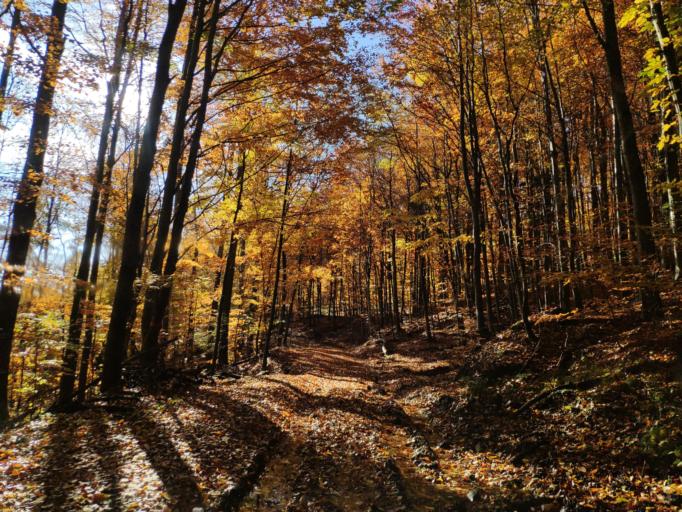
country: SK
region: Kosicky
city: Moldava nad Bodvou
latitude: 48.7340
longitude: 21.0257
